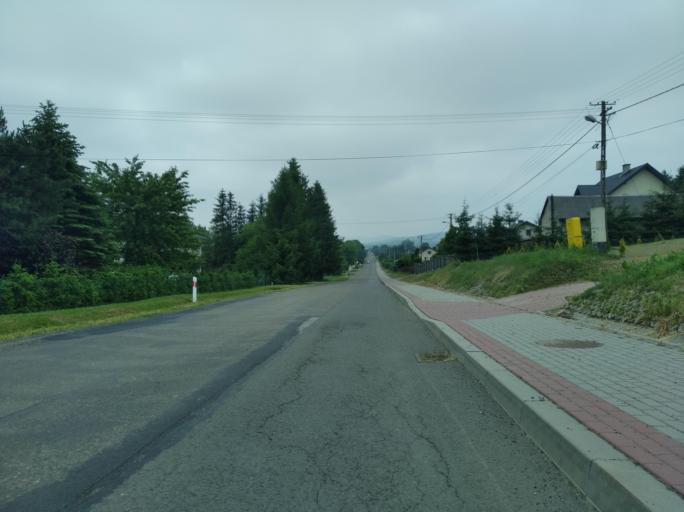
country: PL
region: Subcarpathian Voivodeship
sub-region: Powiat krosnienski
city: Sieniawa
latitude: 49.5771
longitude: 21.9236
